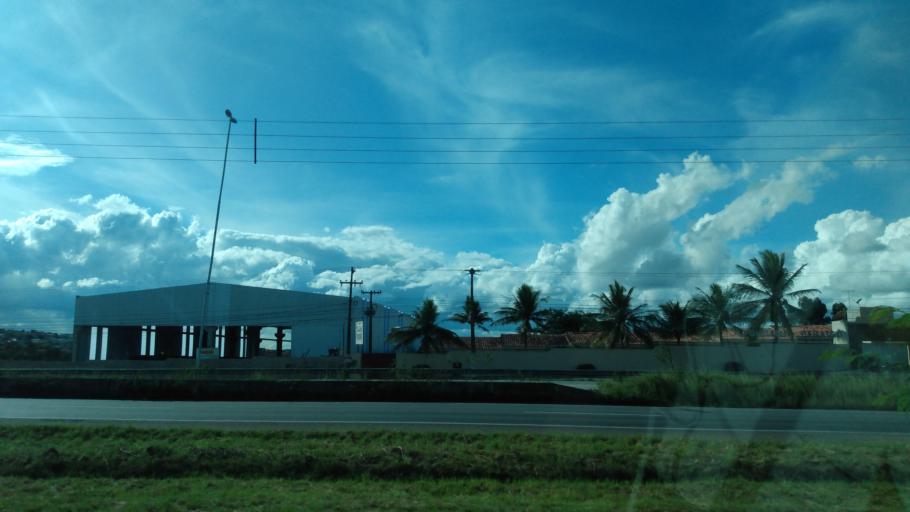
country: ET
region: Oromiya
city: Gore
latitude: 8.1980
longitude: 35.5832
